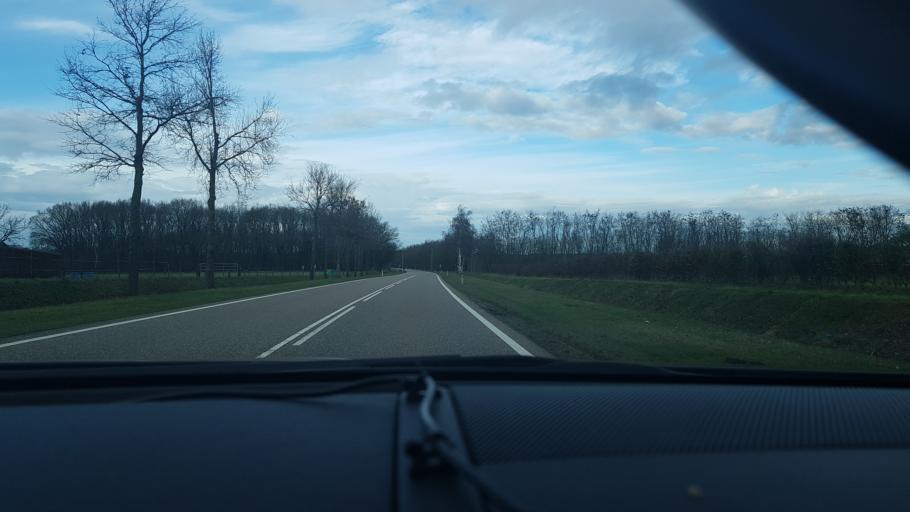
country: NL
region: Limburg
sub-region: Gemeente Beesel
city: Reuver
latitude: 51.3074
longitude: 6.0557
